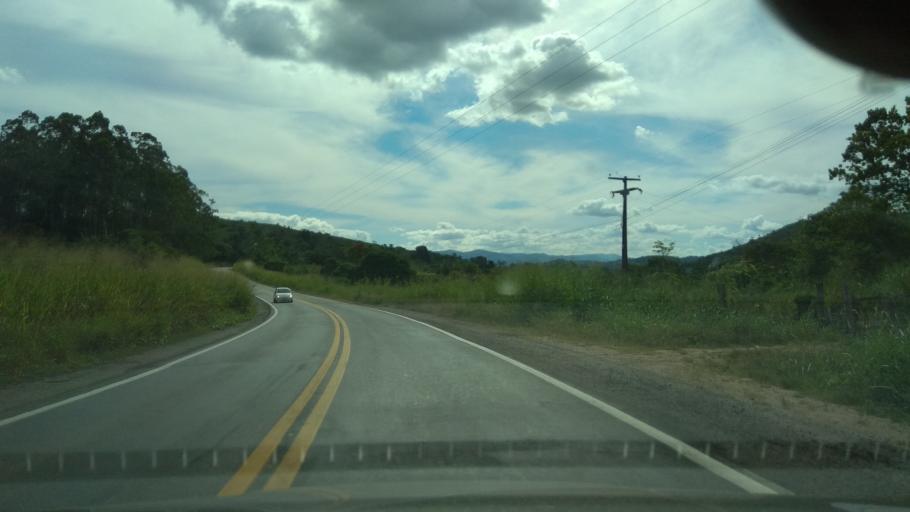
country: BR
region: Bahia
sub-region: Ipiau
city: Ipiau
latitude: -14.0744
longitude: -39.7851
